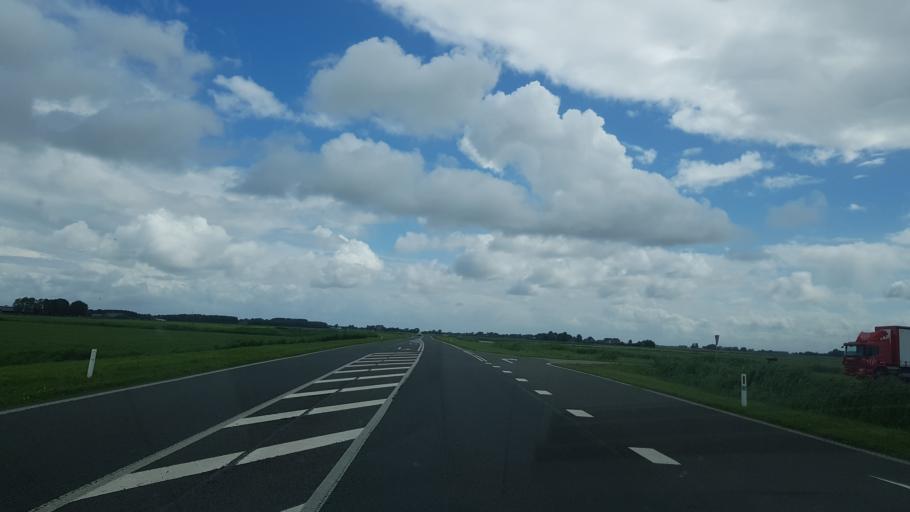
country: NL
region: Friesland
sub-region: Gemeente Dantumadiel
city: Walterswald
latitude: 53.3409
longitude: 6.0476
